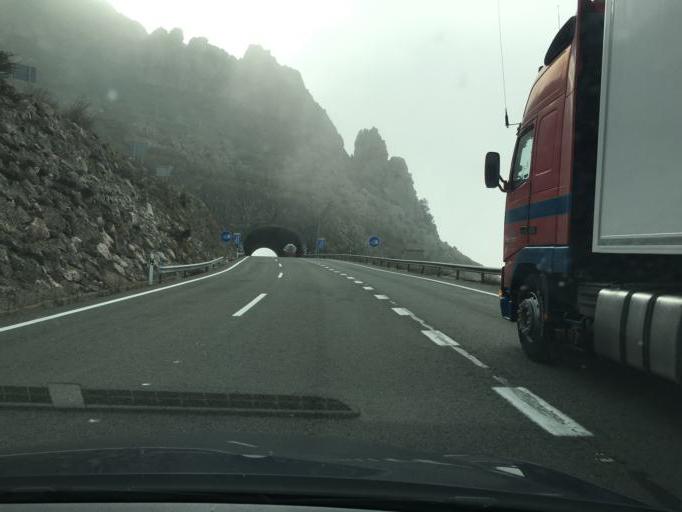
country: ES
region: Castille and Leon
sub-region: Provincia de Burgos
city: Pancorbo
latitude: 42.6362
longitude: -3.1077
